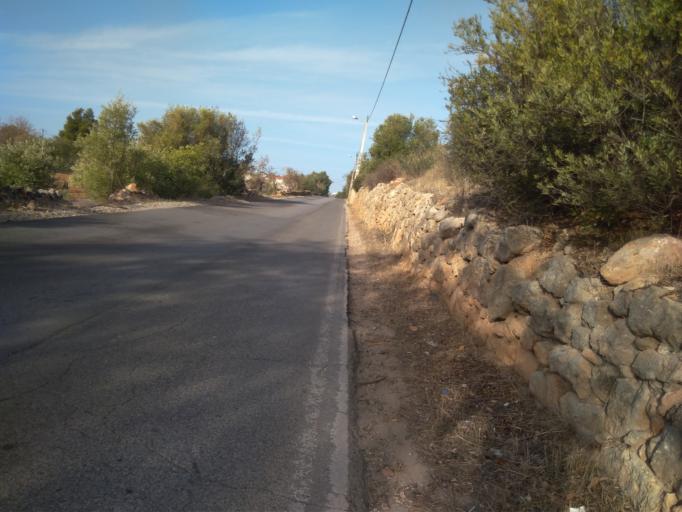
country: PT
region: Faro
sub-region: Faro
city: Santa Barbara de Nexe
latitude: 37.0990
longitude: -7.9591
